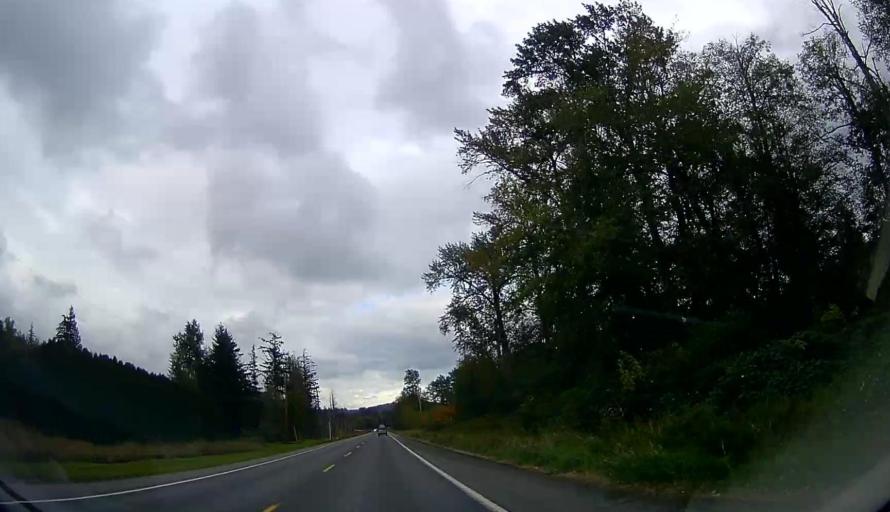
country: US
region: Washington
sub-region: Skagit County
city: Sedro-Woolley
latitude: 48.5277
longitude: -122.1682
